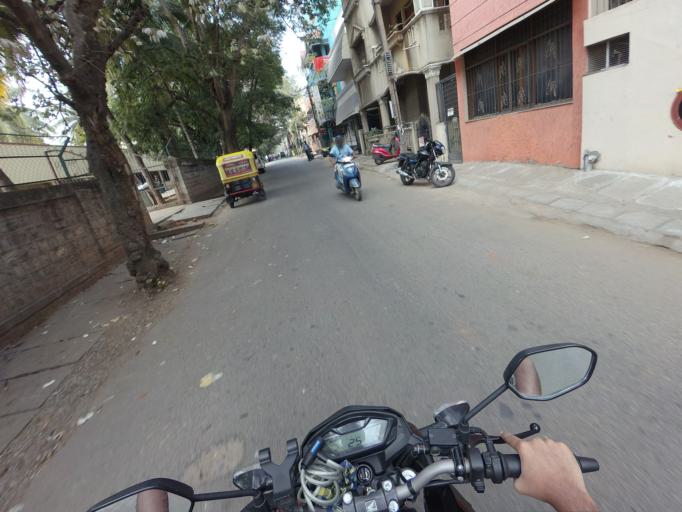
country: IN
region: Karnataka
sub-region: Bangalore Urban
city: Bangalore
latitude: 12.9699
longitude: 77.5444
